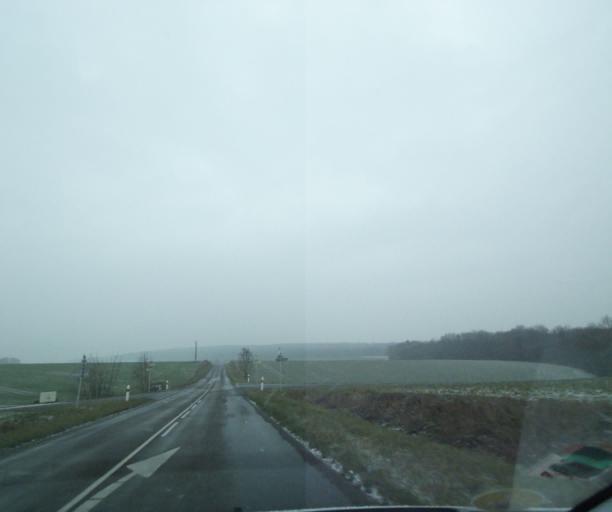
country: FR
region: Champagne-Ardenne
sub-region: Departement de la Haute-Marne
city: Wassy
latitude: 48.4812
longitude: 4.9992
